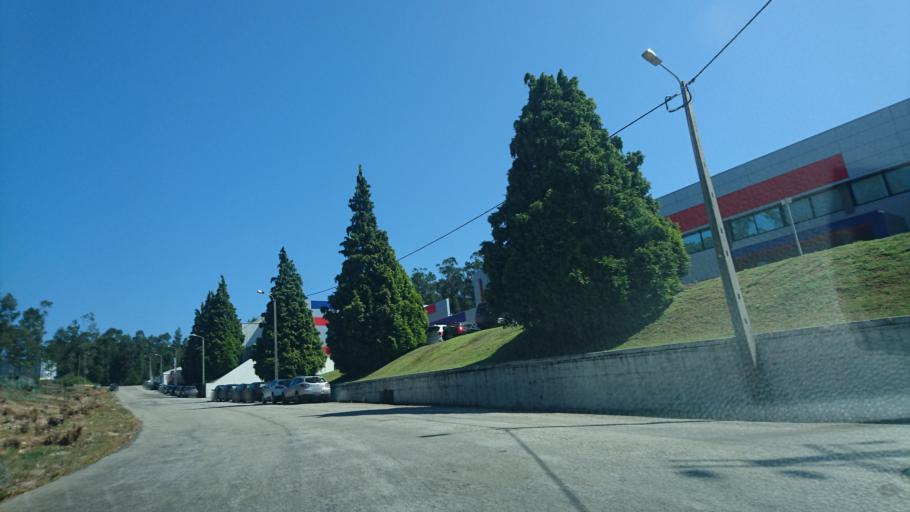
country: PT
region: Aveiro
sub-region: Oliveira de Azemeis
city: Vila Cha
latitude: 40.8856
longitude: -8.4288
